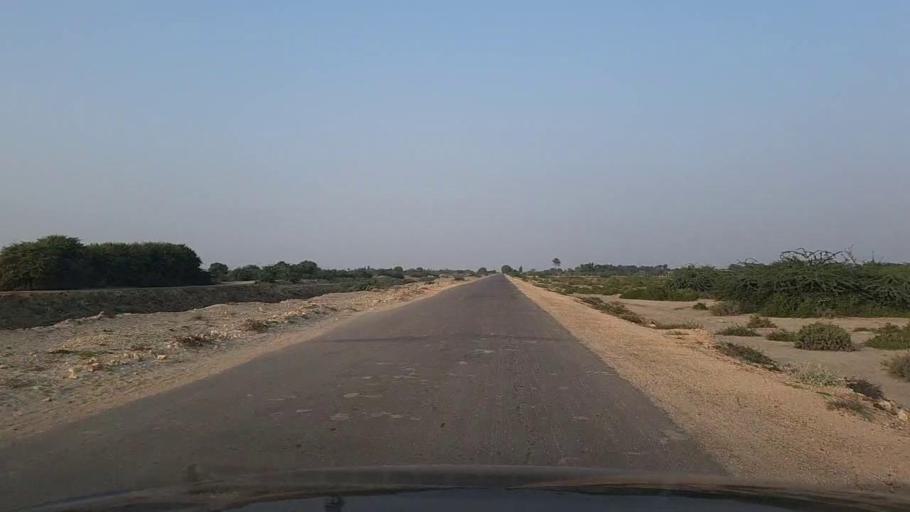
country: PK
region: Sindh
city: Mirpur Sakro
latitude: 24.4908
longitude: 67.8095
